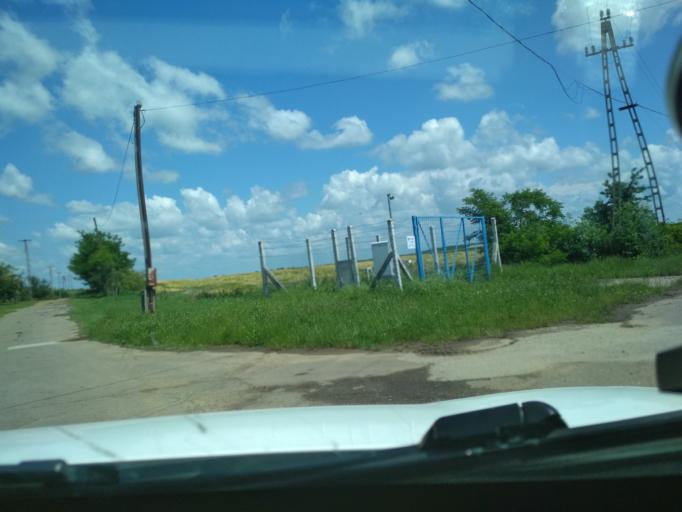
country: HU
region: Jasz-Nagykun-Szolnok
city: Abadszalok
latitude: 47.4788
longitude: 20.6171
